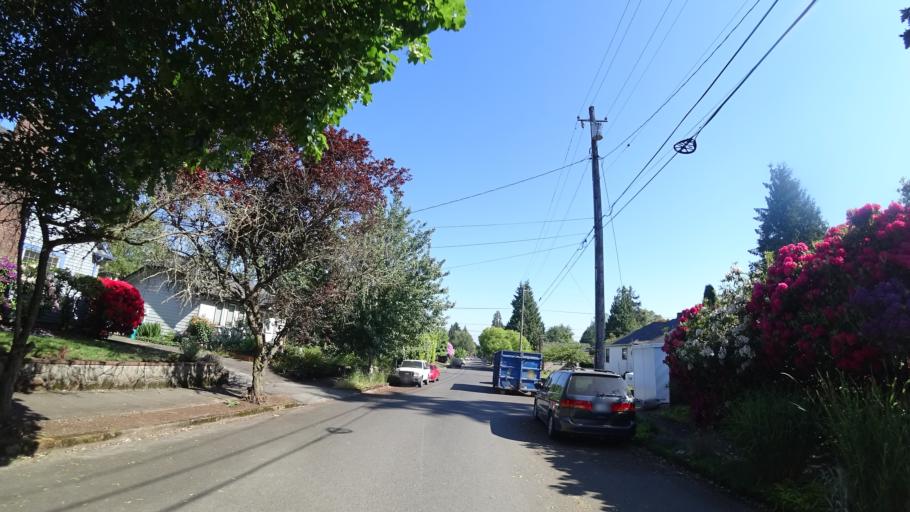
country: US
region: Oregon
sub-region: Multnomah County
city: Portland
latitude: 45.5753
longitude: -122.6634
